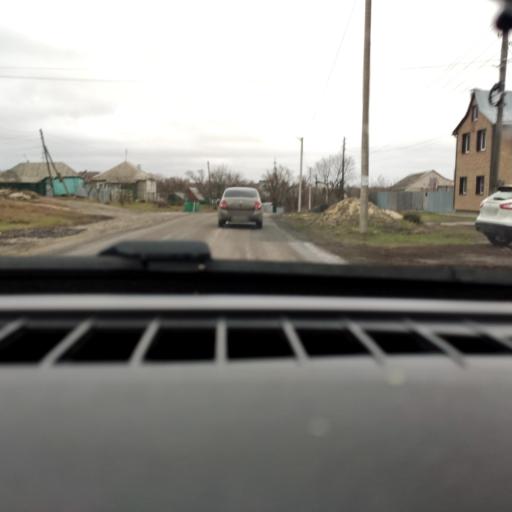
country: RU
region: Voronezj
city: Devitsa
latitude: 51.6399
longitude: 38.9375
